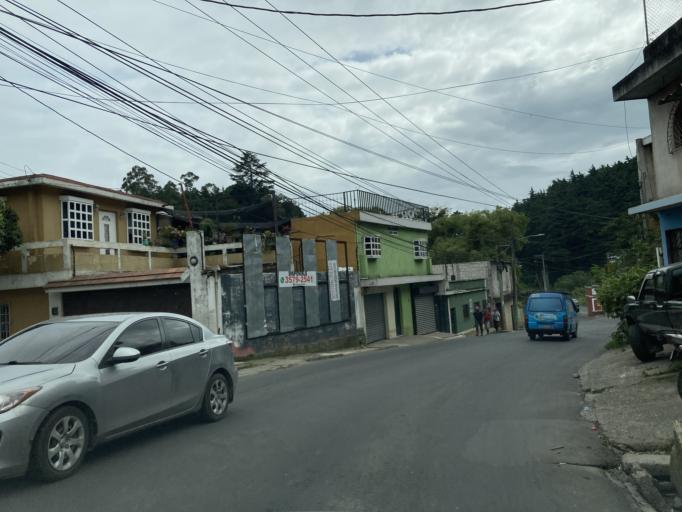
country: GT
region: Guatemala
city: San Jose Pinula
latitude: 14.5373
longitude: -90.4069
